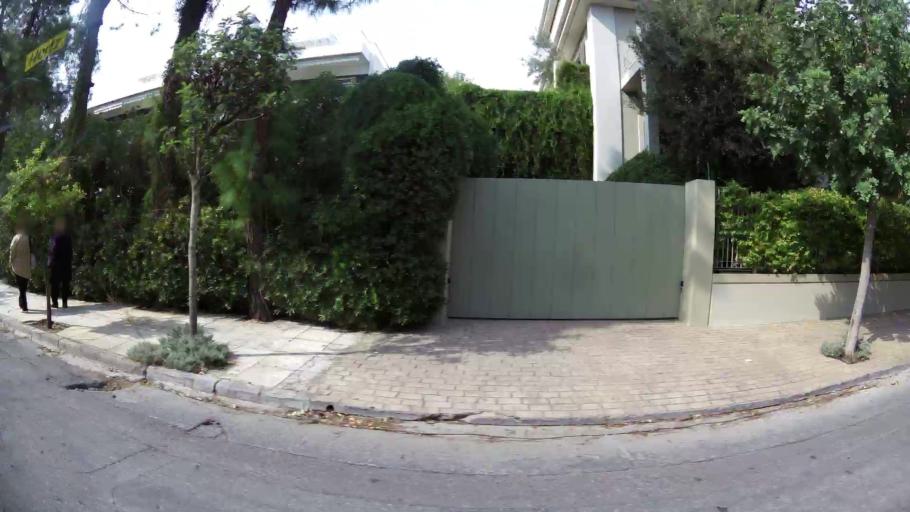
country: GR
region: Attica
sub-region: Nomarchia Athinas
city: Psychiko
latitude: 38.0043
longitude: 23.7716
